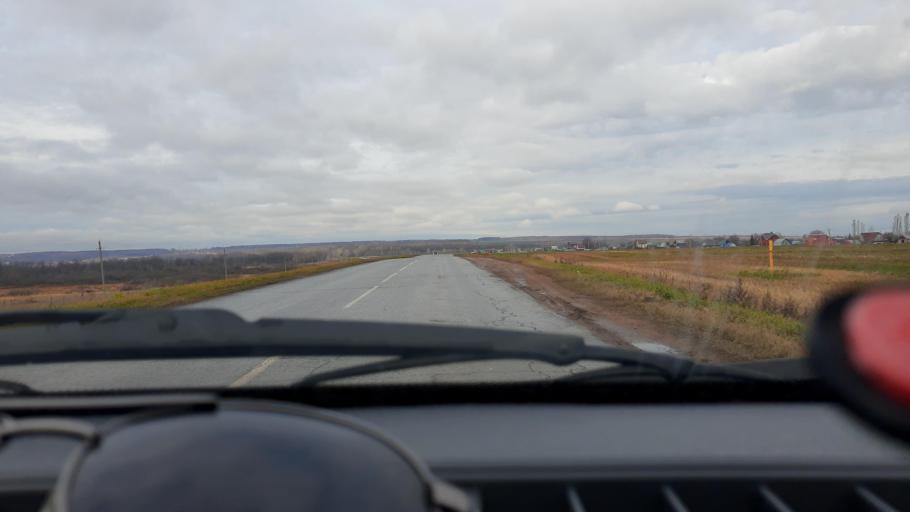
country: RU
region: Bashkortostan
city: Mikhaylovka
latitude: 54.8296
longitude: 55.9646
